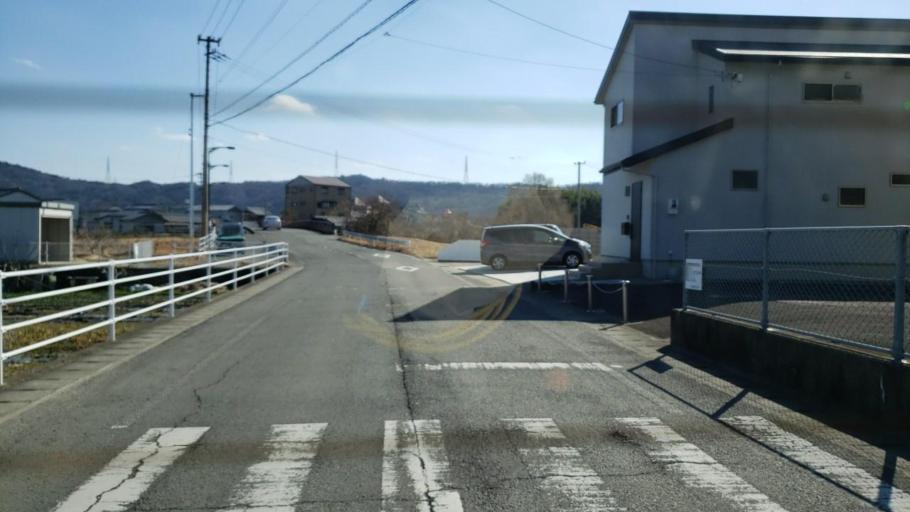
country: JP
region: Tokushima
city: Ishii
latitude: 34.0693
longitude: 134.4357
